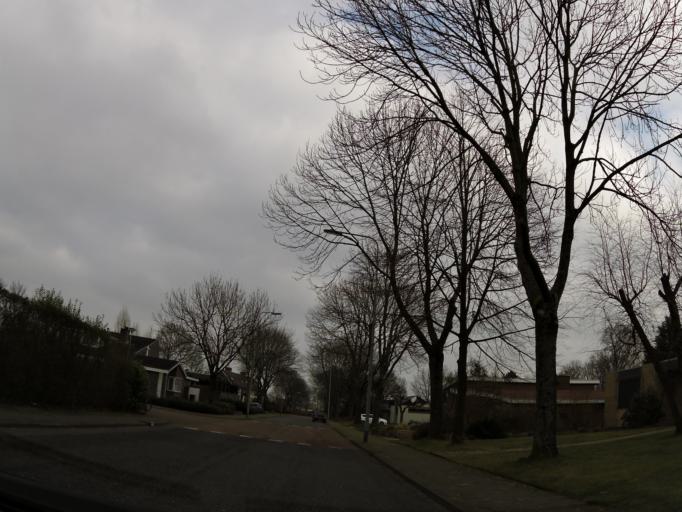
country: NL
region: Limburg
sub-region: Gemeente Kerkrade
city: Kerkrade
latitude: 50.9126
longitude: 6.0571
